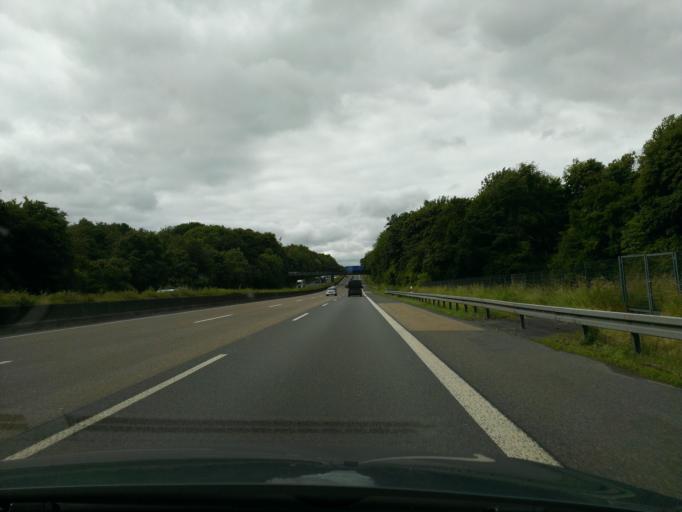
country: DE
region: North Rhine-Westphalia
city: Burscheid
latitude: 51.0957
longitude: 7.1395
